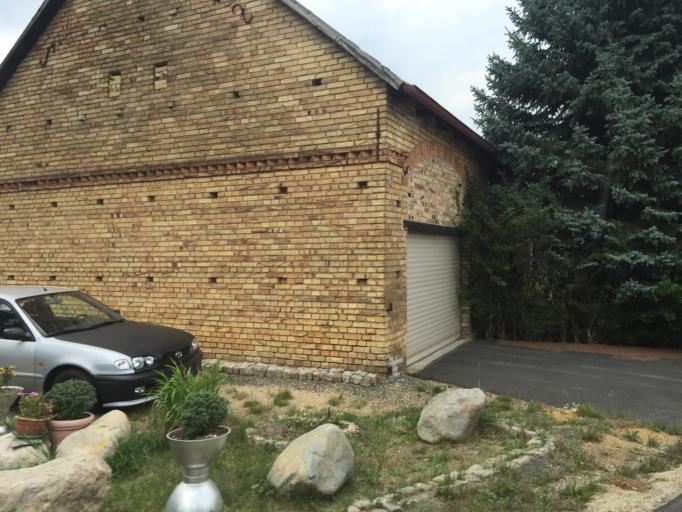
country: DE
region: Saxony
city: Trebendorf
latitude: 51.5247
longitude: 14.5616
